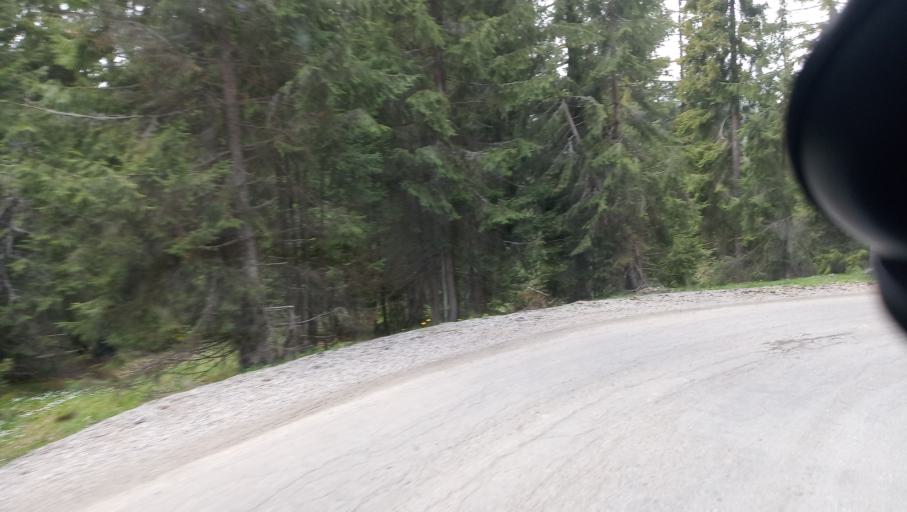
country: RO
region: Alba
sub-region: Comuna Horea
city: Horea
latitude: 46.5477
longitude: 22.8955
